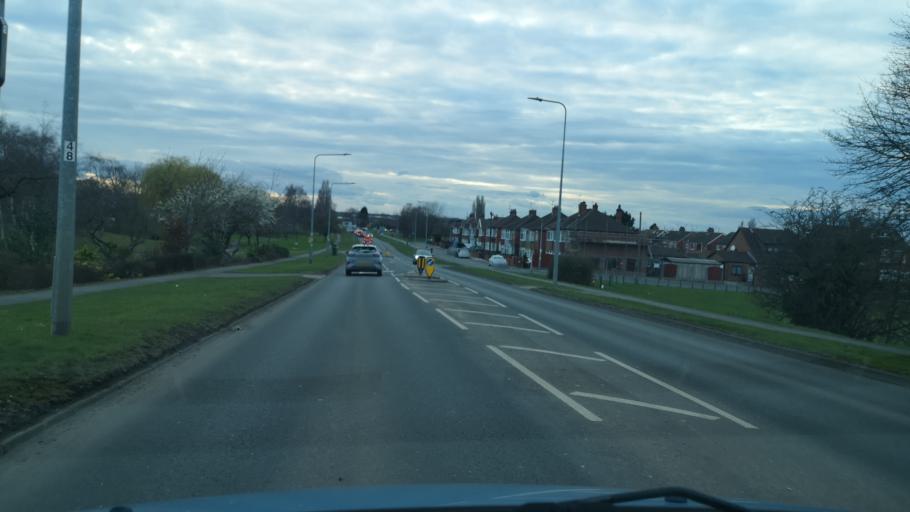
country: GB
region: England
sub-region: North Lincolnshire
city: Scunthorpe
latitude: 53.5900
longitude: -0.6768
